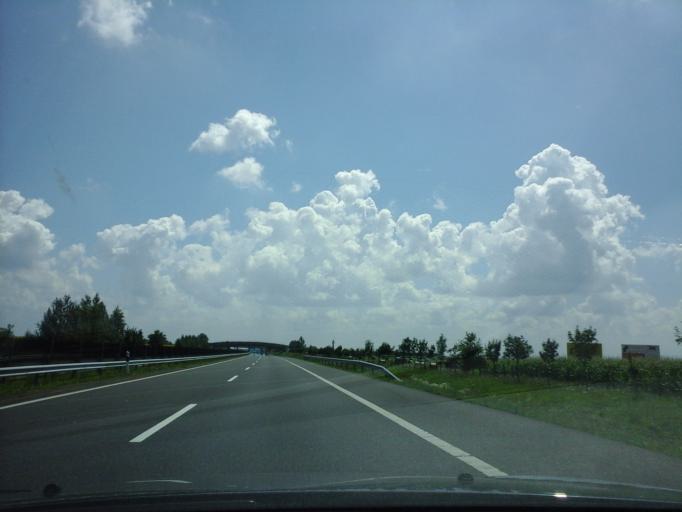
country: HU
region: Hajdu-Bihar
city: Hajduboszormeny
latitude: 47.5865
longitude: 21.5295
